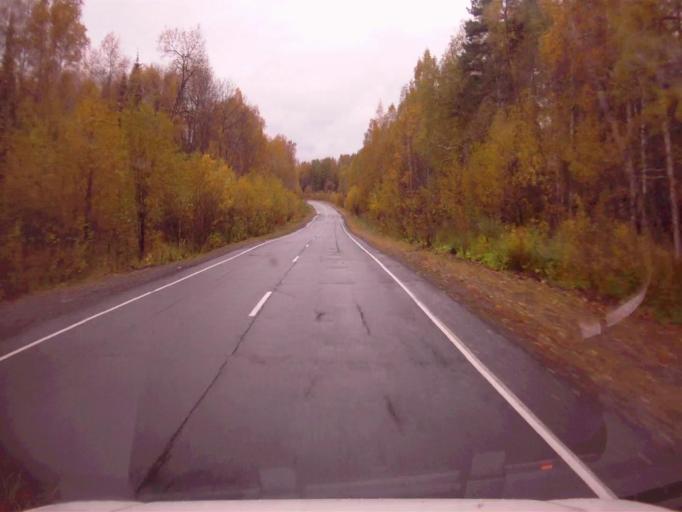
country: RU
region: Chelyabinsk
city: Nizhniy Ufaley
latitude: 56.0673
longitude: 60.0115
